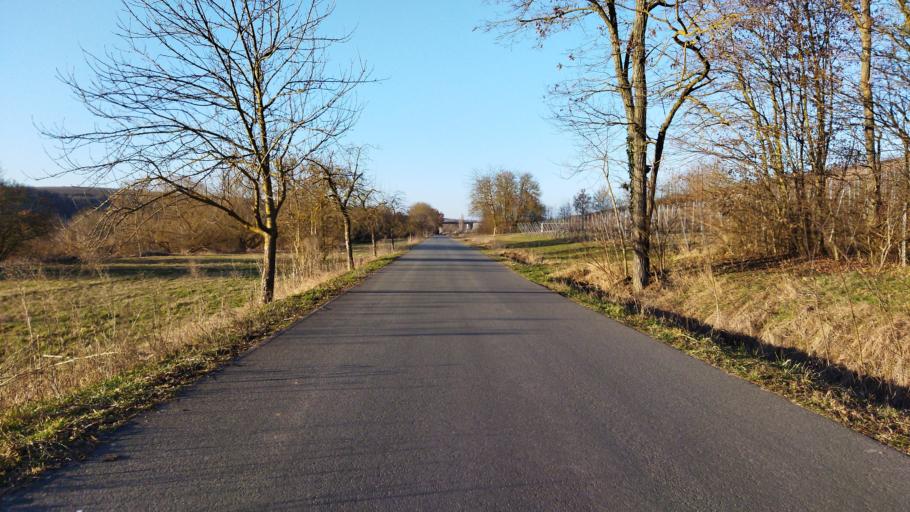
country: DE
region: Bavaria
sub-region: Regierungsbezirk Unterfranken
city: Mainstockheim
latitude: 49.7778
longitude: 10.1570
